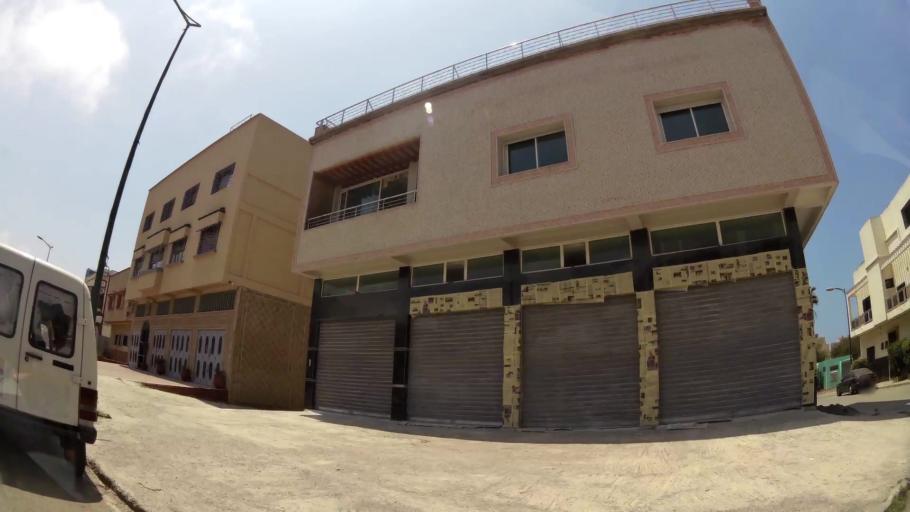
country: MA
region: Rabat-Sale-Zemmour-Zaer
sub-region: Skhirate-Temara
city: Temara
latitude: 33.9782
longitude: -6.8948
